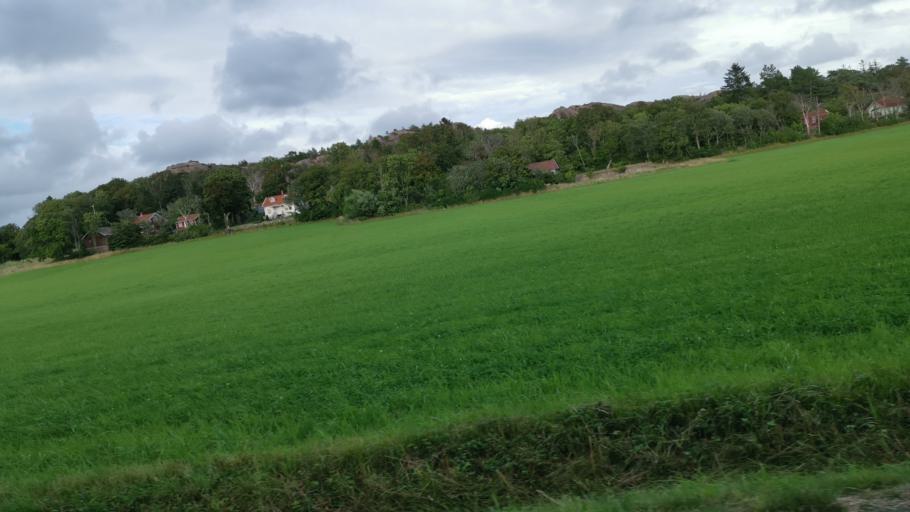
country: SE
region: Vaestra Goetaland
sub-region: Sotenas Kommun
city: Hunnebostrand
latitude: 58.5177
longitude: 11.3054
